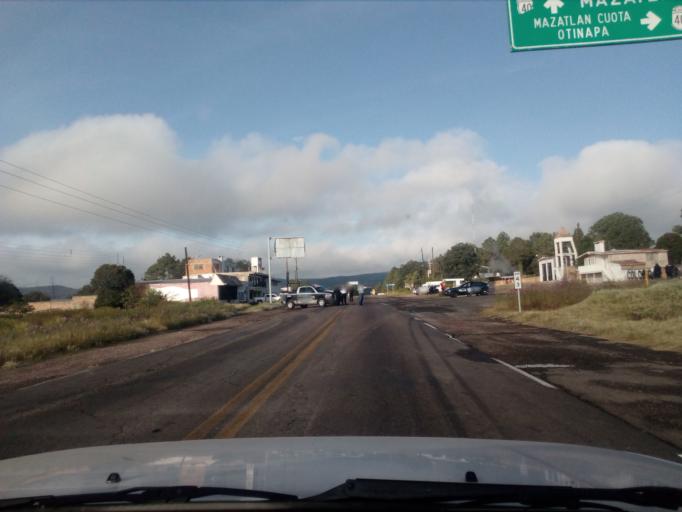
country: MX
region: Durango
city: Victoria de Durango
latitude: 23.9252
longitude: -104.9398
